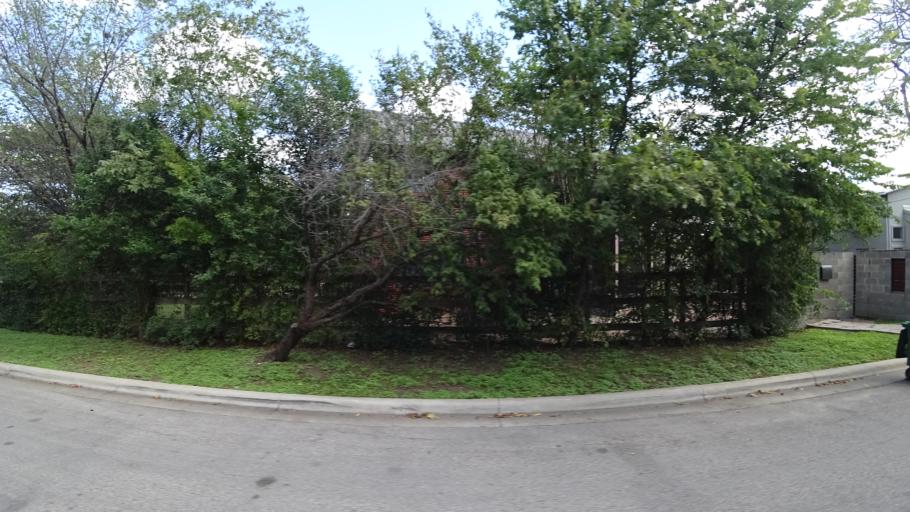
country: US
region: Texas
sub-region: Travis County
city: Austin
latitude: 30.3102
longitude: -97.7162
